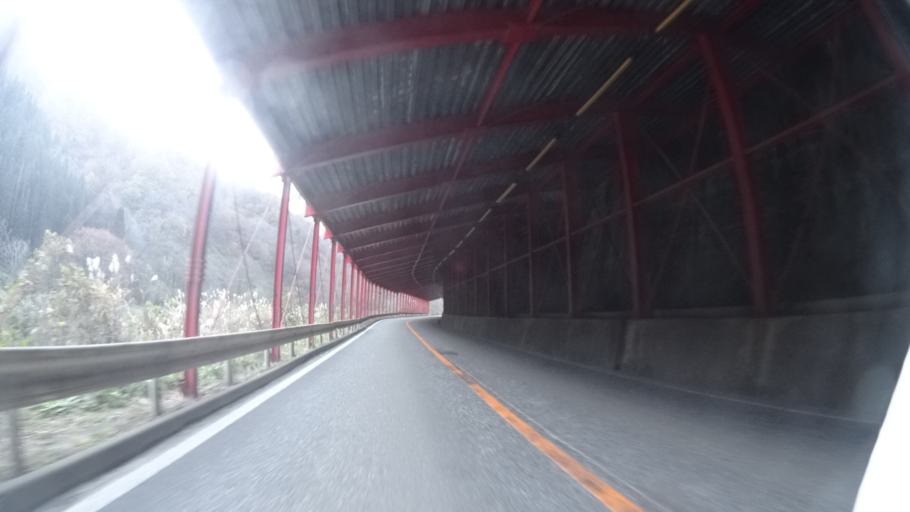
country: JP
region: Fukui
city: Ono
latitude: 35.9098
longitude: 136.6328
